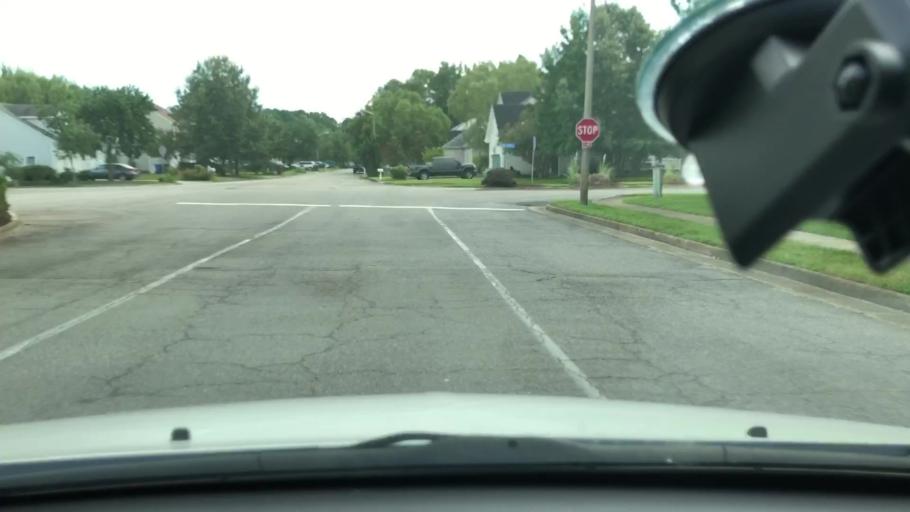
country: US
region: Virginia
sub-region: City of Chesapeake
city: Chesapeake
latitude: 36.7147
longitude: -76.2890
